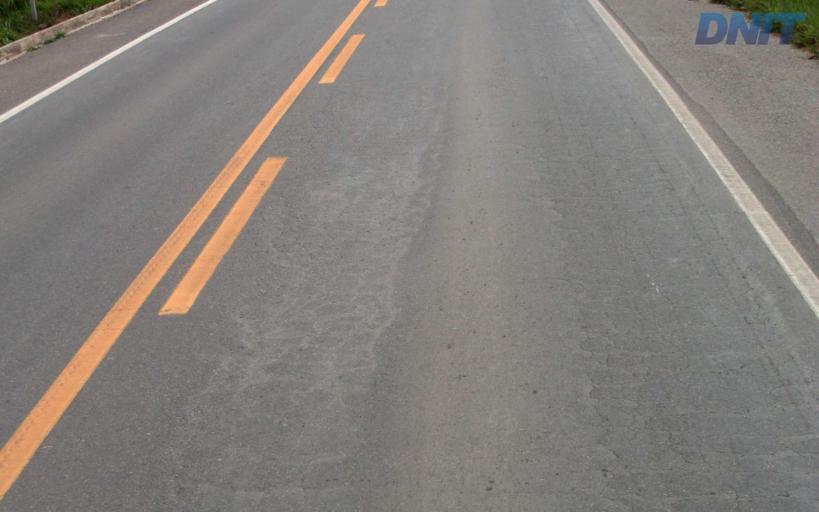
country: BR
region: Minas Gerais
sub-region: Governador Valadares
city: Governador Valadares
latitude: -18.9753
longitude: -42.0971
